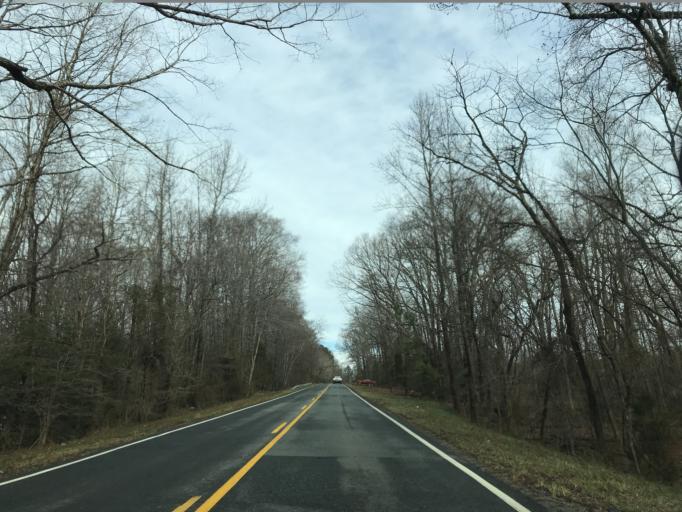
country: US
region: Virginia
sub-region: King George County
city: Dahlgren
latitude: 38.2696
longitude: -77.0462
